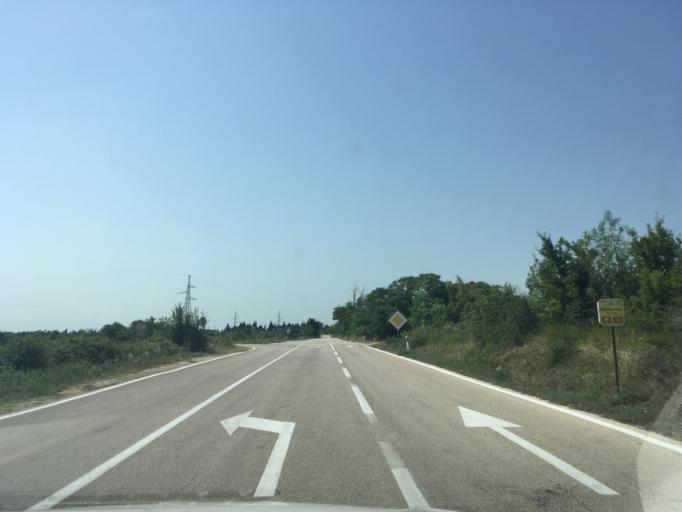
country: HR
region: Zadarska
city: Benkovac
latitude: 44.0239
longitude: 15.6336
